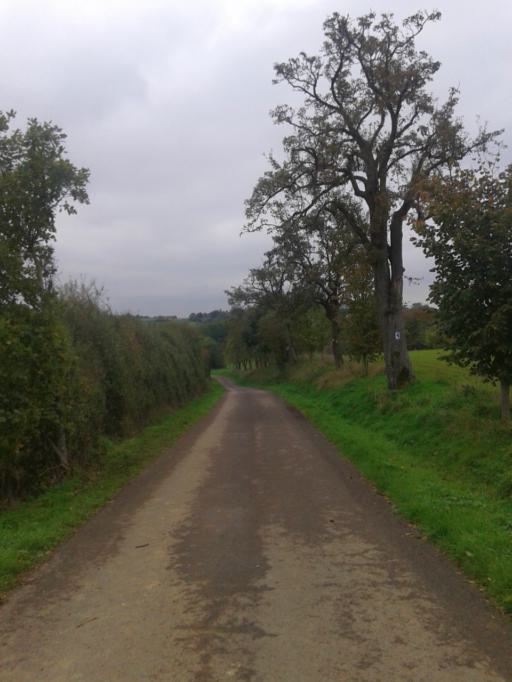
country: LU
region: Luxembourg
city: Bergem
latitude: 49.5332
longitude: 6.0700
